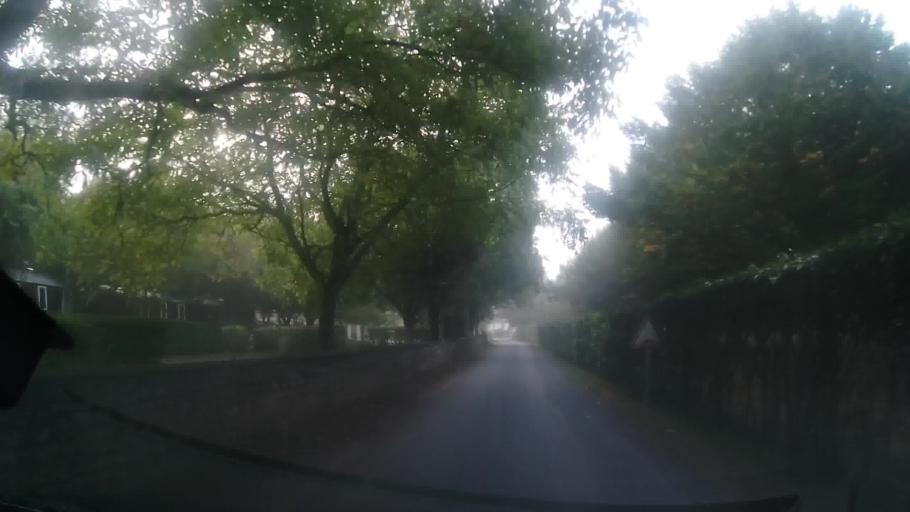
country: FR
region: Aquitaine
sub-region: Departement de la Dordogne
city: Cenac-et-Saint-Julien
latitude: 44.8058
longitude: 1.1579
